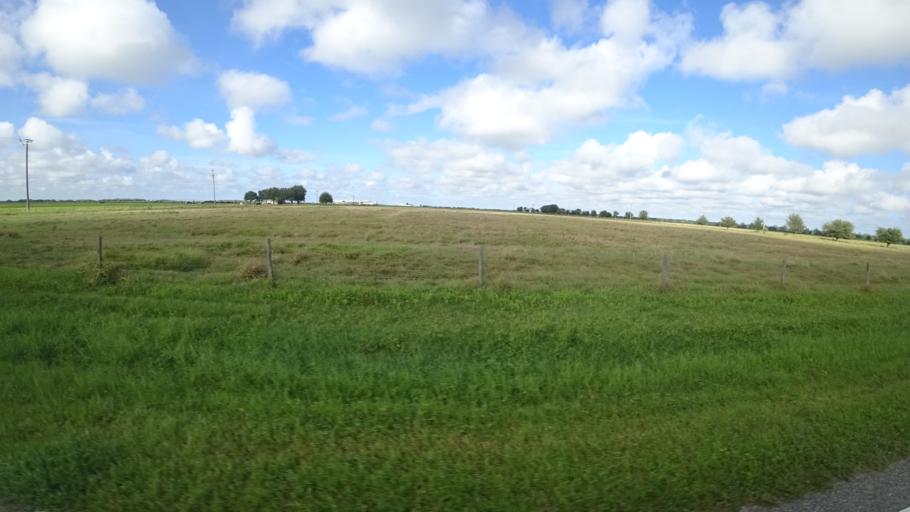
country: US
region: Florida
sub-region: Sarasota County
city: Lake Sarasota
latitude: 27.3707
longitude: -82.2683
